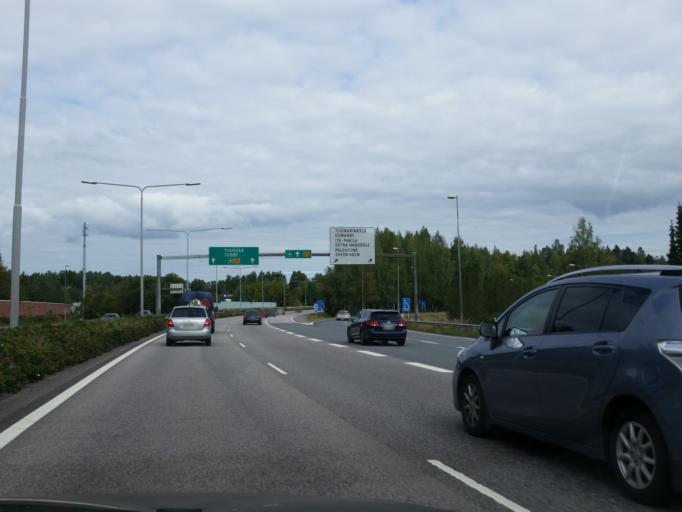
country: FI
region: Uusimaa
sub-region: Helsinki
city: Helsinki
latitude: 60.2523
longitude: 24.9486
